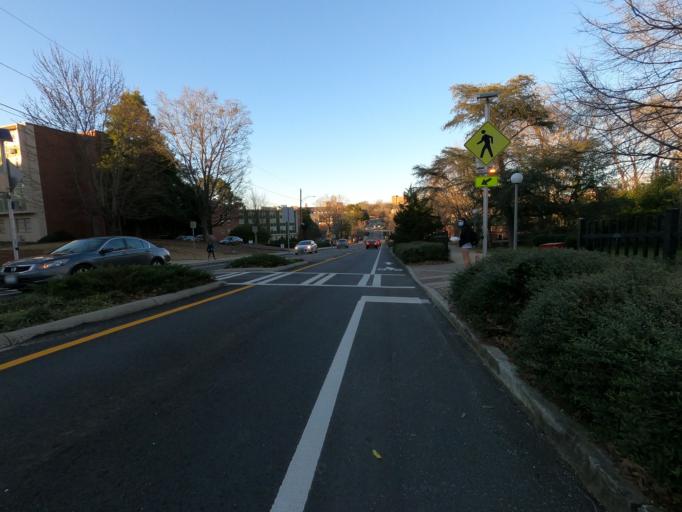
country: US
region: Georgia
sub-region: Clarke County
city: Athens
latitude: 33.9485
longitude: -83.3777
